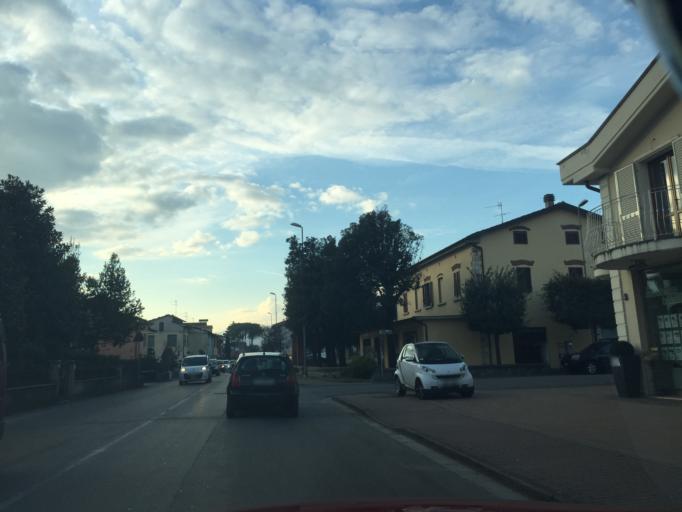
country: IT
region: Tuscany
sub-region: Provincia di Pistoia
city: Monsummano Terme
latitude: 43.8718
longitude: 10.8102
